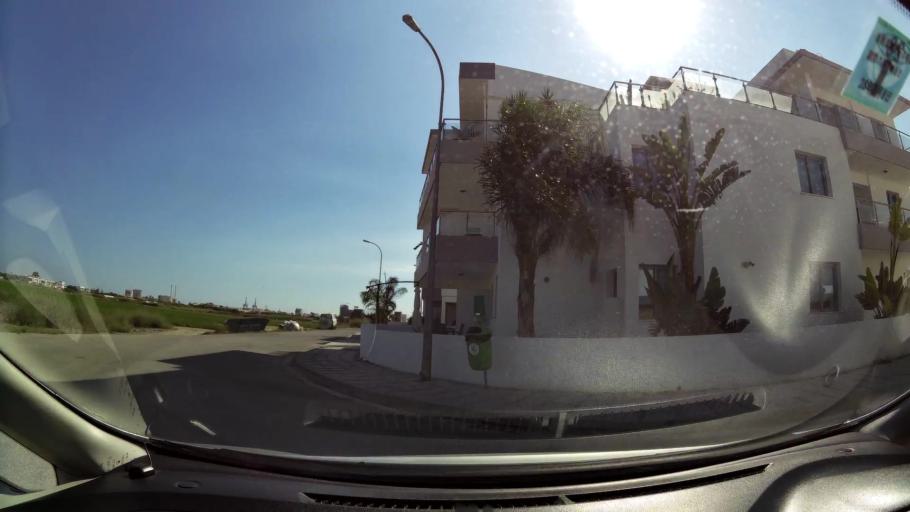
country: CY
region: Larnaka
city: Livadia
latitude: 34.9473
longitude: 33.6373
